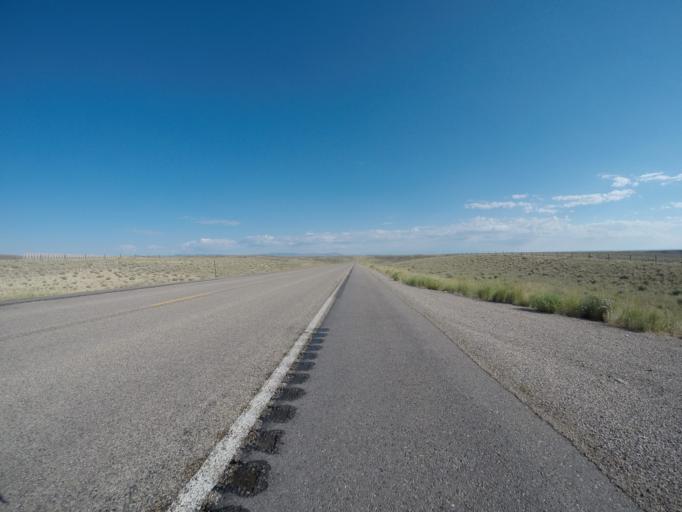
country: US
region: Wyoming
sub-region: Lincoln County
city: Kemmerer
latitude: 42.0400
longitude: -110.1579
